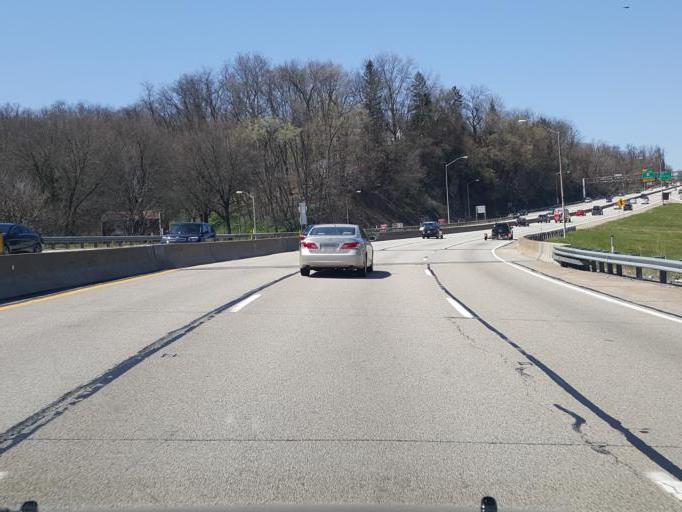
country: US
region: Pennsylvania
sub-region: Allegheny County
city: Churchill
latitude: 40.4409
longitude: -79.8338
